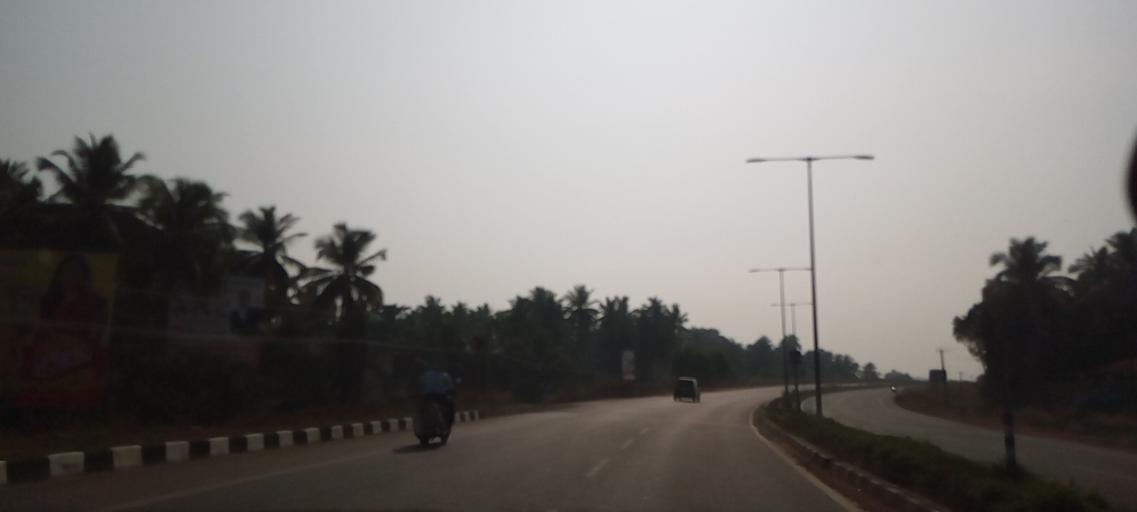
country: IN
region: Karnataka
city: Gangolli
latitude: 13.6884
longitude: 74.6780
